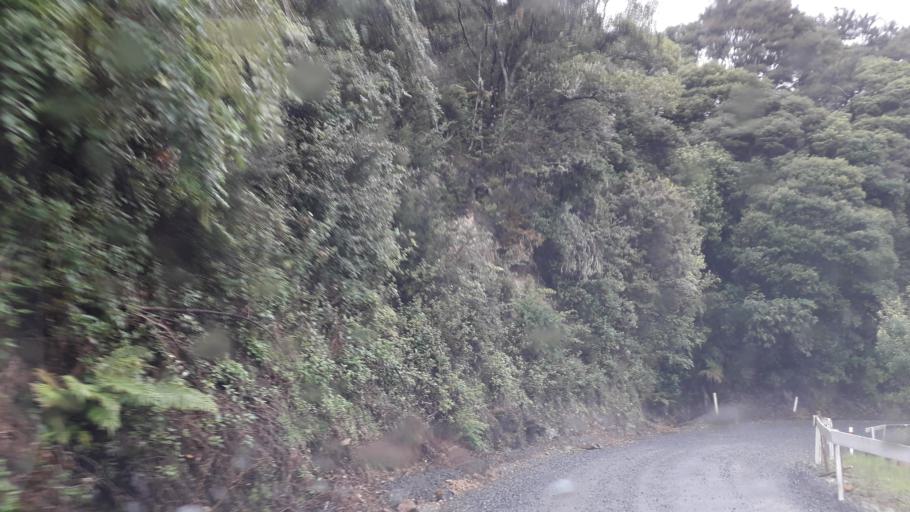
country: NZ
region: Northland
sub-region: Far North District
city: Kerikeri
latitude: -35.1316
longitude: 173.7191
